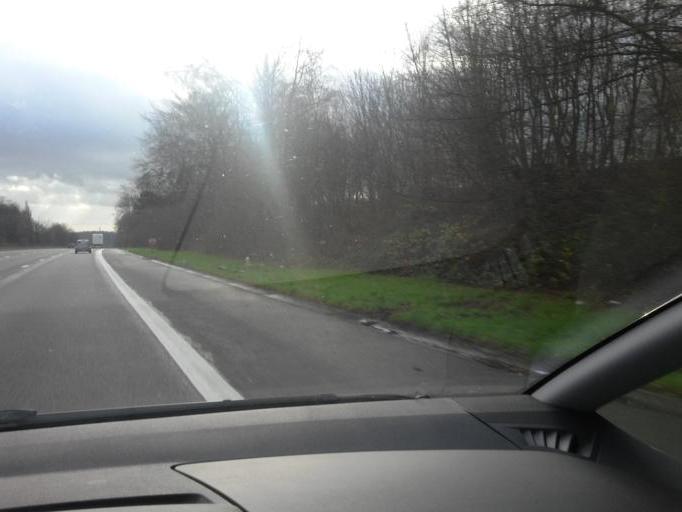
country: BE
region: Flanders
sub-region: Provincie Vlaams-Brabant
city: Hoeilaart
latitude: 50.7804
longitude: 4.4978
